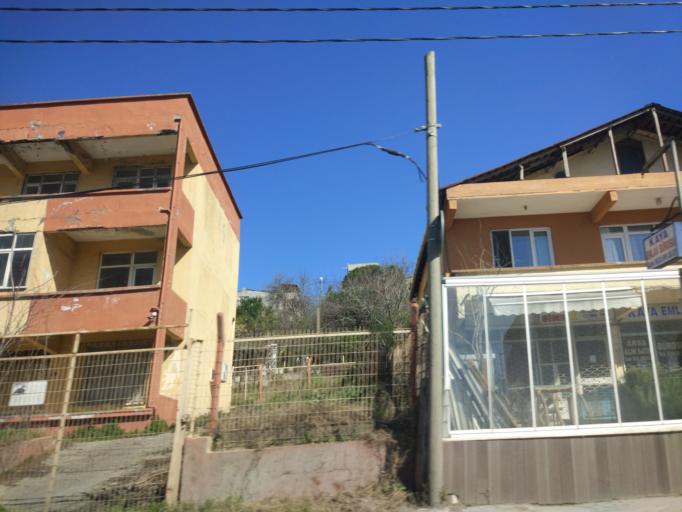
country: TR
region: Istanbul
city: Basaksehir
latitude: 41.0574
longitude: 28.7491
